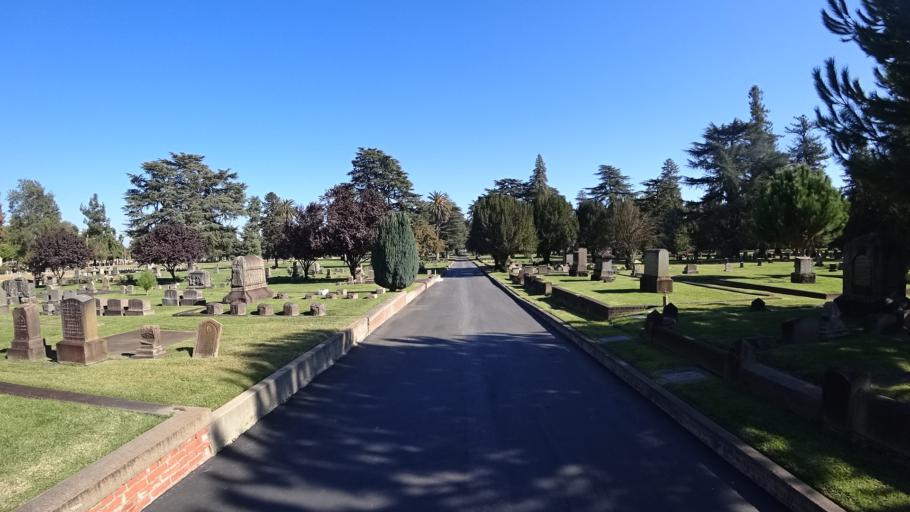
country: US
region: California
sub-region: Sacramento County
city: Sacramento
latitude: 38.5601
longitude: -121.5033
